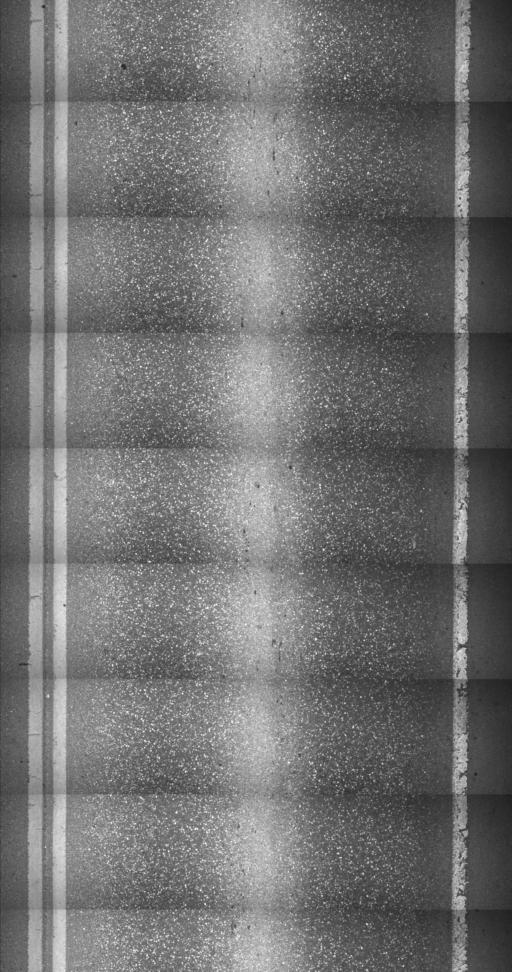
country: US
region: Vermont
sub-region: Chittenden County
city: Hinesburg
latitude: 44.3394
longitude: -73.1153
